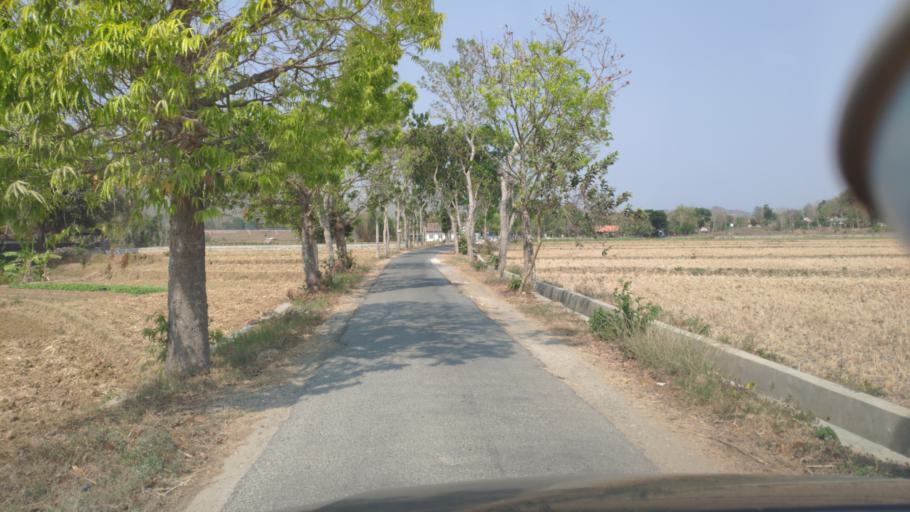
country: ID
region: Central Java
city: Tempuran
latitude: -6.9120
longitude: 111.4563
